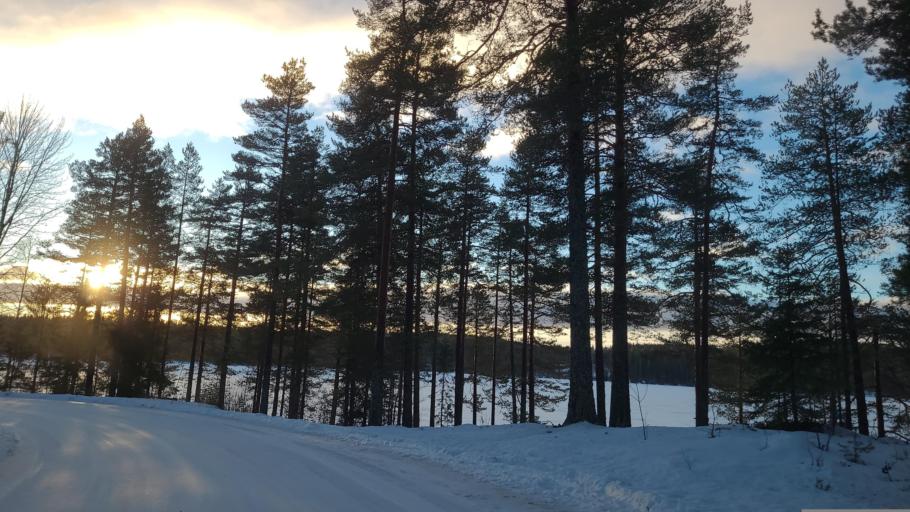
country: SE
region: Gaevleborg
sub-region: Bollnas Kommun
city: Kilafors
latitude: 61.3900
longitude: 16.6847
